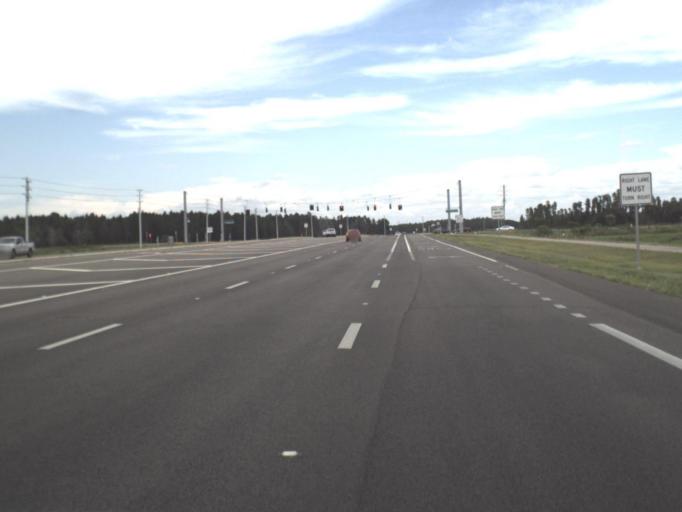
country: US
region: Florida
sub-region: Pasco County
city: Wesley Chapel
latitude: 28.1965
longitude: -82.3320
